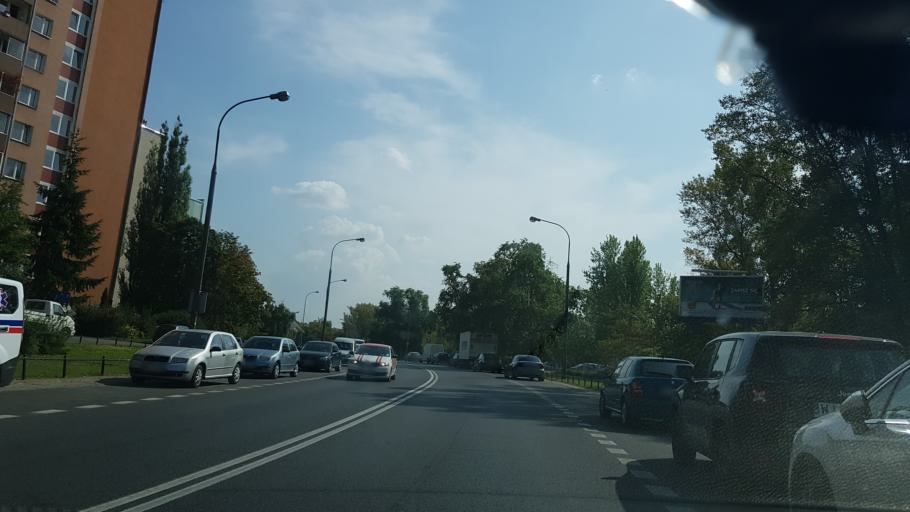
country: PL
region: Masovian Voivodeship
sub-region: Warszawa
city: Bielany
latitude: 52.2746
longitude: 20.9234
